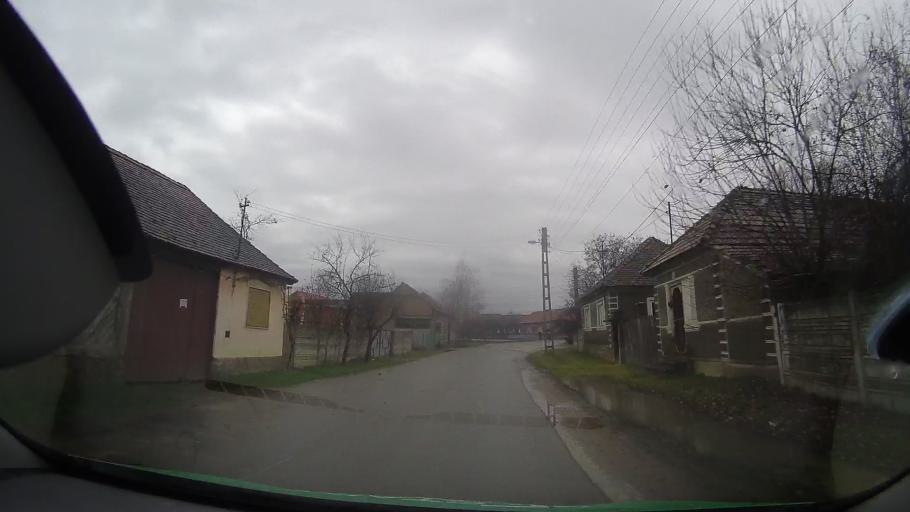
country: RO
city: Capalna
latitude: 46.7092
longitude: 22.0546
